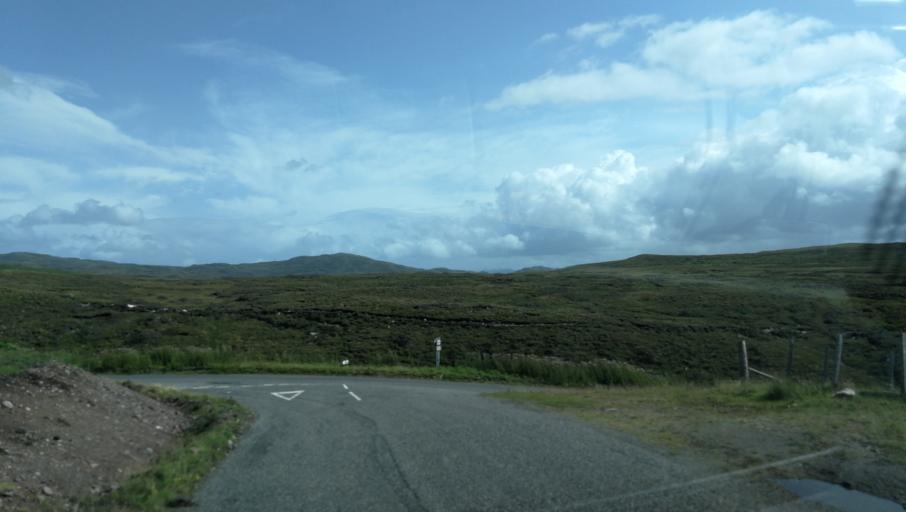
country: GB
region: Scotland
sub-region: Highland
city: Portree
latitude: 57.7496
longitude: -5.7626
